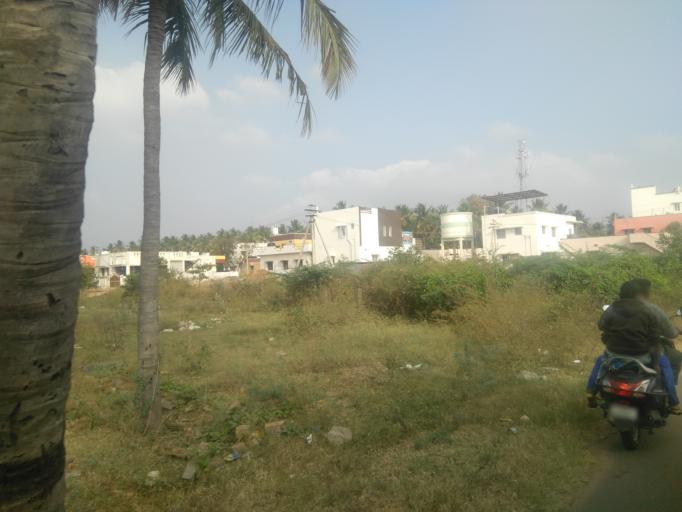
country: IN
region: Tamil Nadu
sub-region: Coimbatore
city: Coimbatore
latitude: 11.0747
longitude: 76.9207
